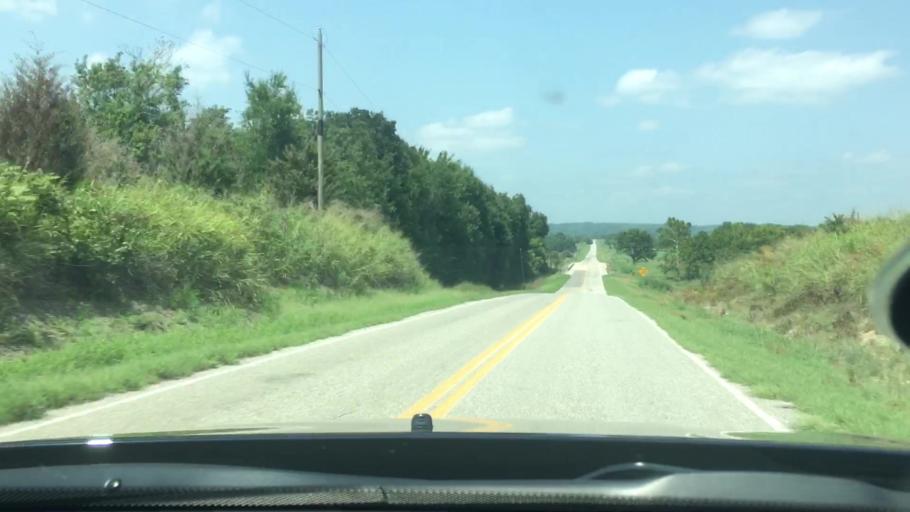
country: US
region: Oklahoma
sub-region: Johnston County
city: Tishomingo
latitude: 34.3870
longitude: -96.4962
